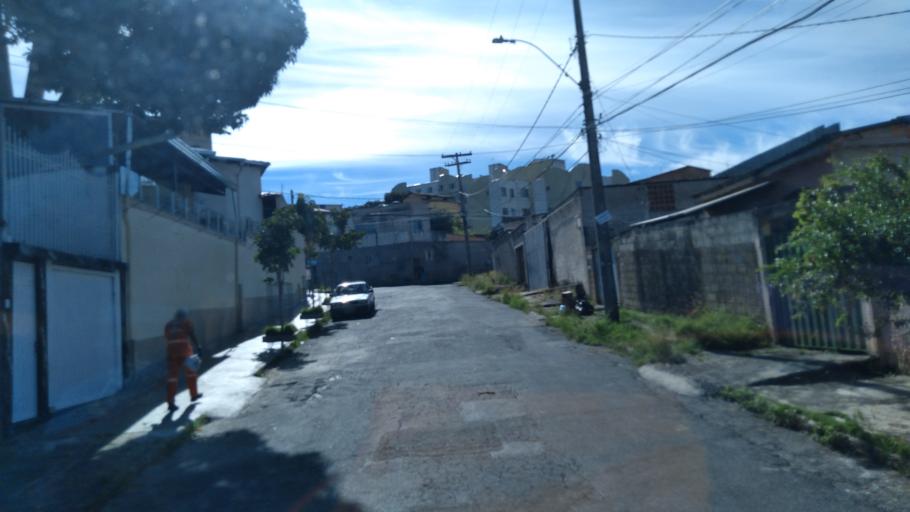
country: BR
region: Minas Gerais
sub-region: Contagem
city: Contagem
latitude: -19.9075
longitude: -44.0013
